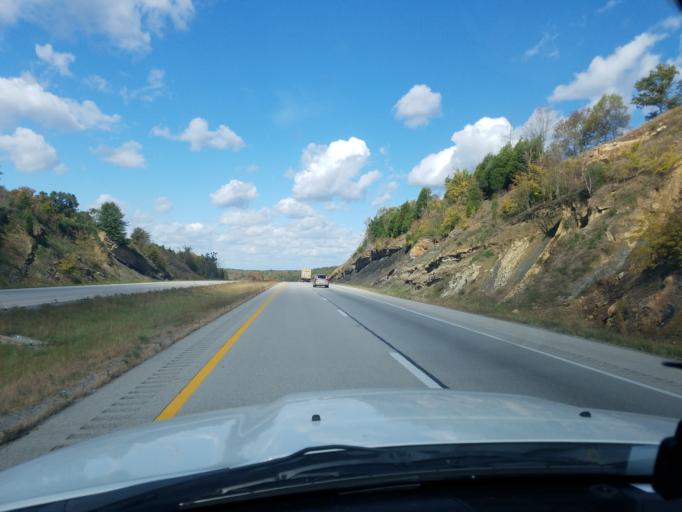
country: US
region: Kentucky
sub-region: Ohio County
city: Hartford
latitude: 37.5251
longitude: -86.9204
